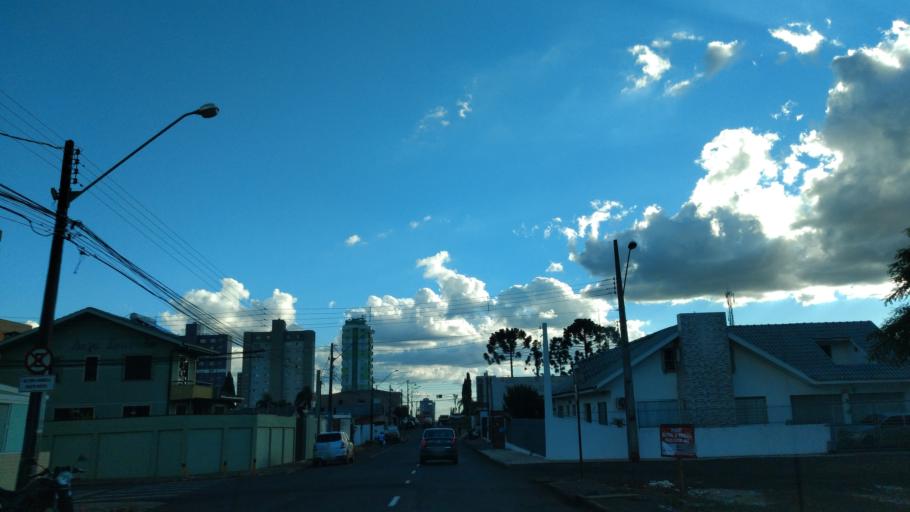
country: BR
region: Parana
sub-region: Guarapuava
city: Guarapuava
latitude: -25.3862
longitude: -51.4616
